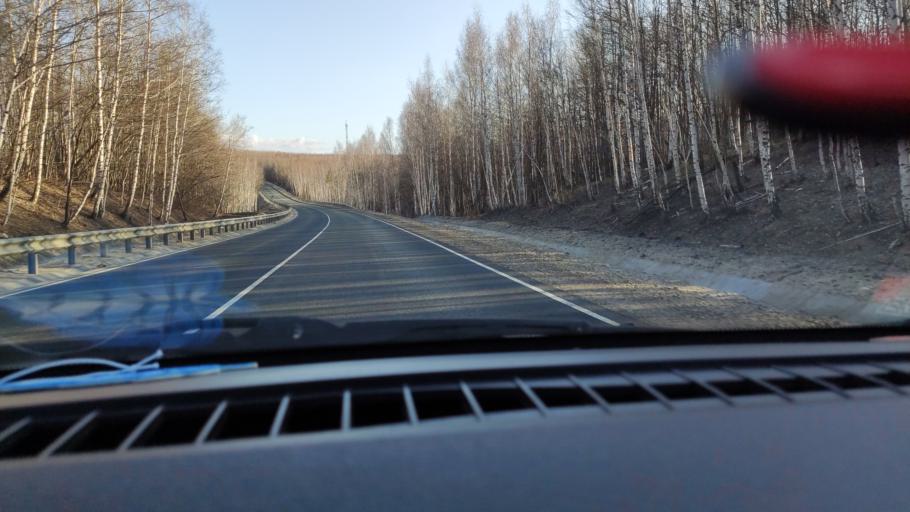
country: RU
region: Saratov
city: Khvalynsk
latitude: 52.4596
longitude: 48.0169
